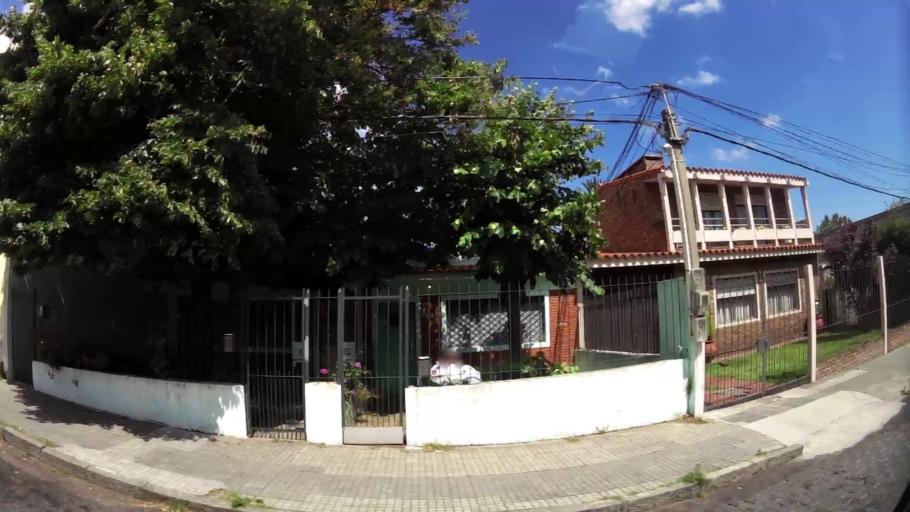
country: UY
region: Montevideo
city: Montevideo
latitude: -34.8577
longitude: -56.2206
